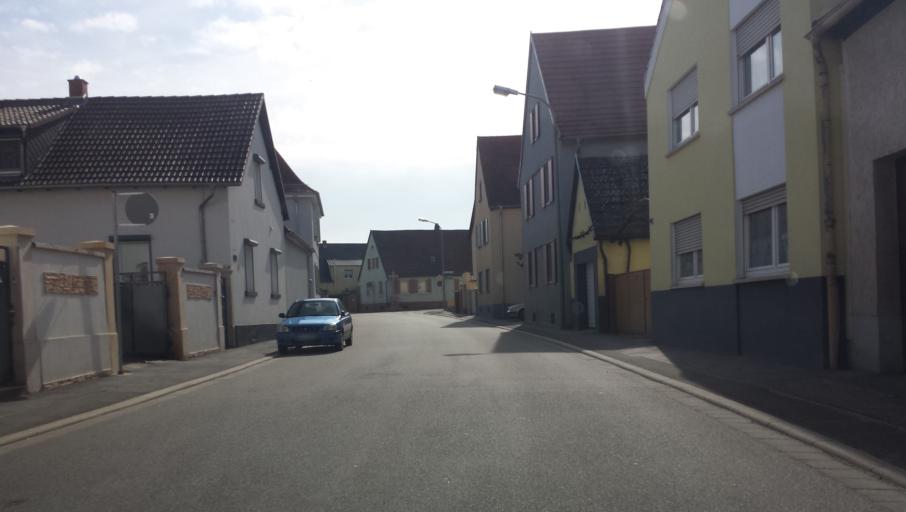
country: DE
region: Rheinland-Pfalz
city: Dudenhofen
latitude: 49.2902
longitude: 8.4082
